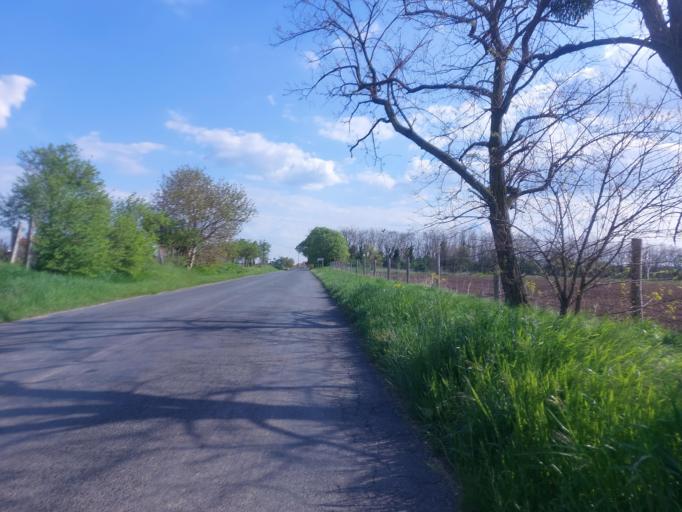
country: HU
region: Veszprem
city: Devecser
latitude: 47.1447
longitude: 17.3552
